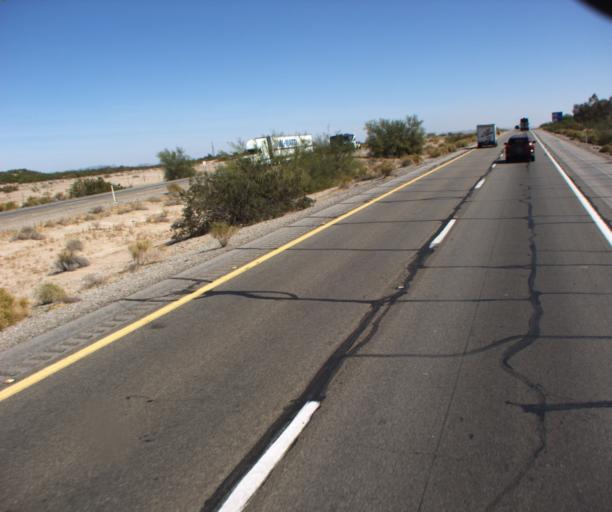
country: US
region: Arizona
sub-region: Yuma County
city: Wellton
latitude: 32.6541
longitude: -114.1744
